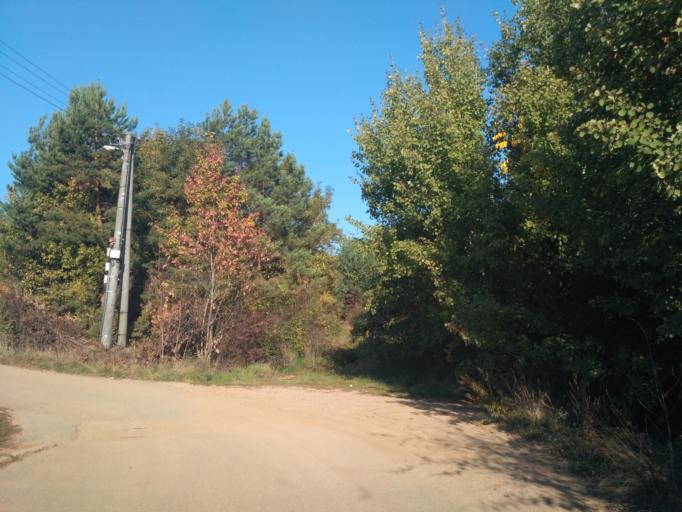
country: SK
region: Kosicky
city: Moldava nad Bodvou
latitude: 48.6179
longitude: 20.9889
